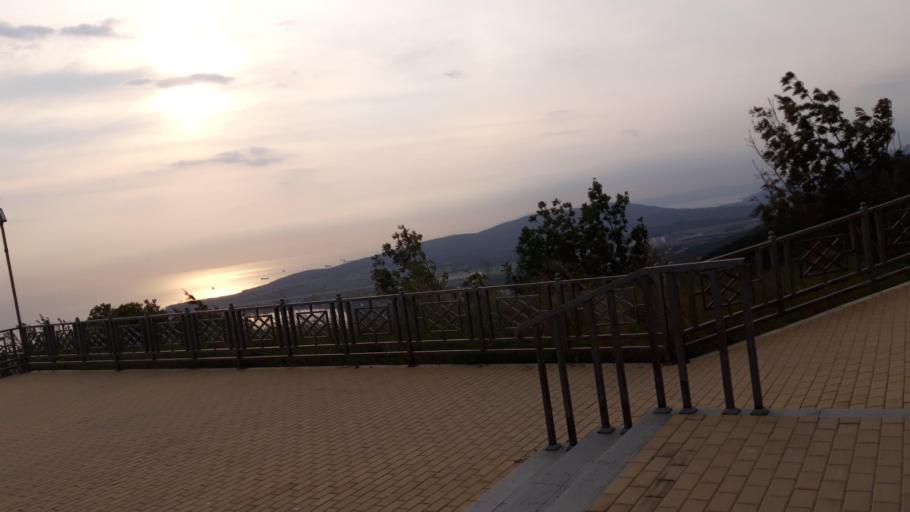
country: RU
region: Krasnodarskiy
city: Gelendzhik
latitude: 44.5851
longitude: 38.0943
